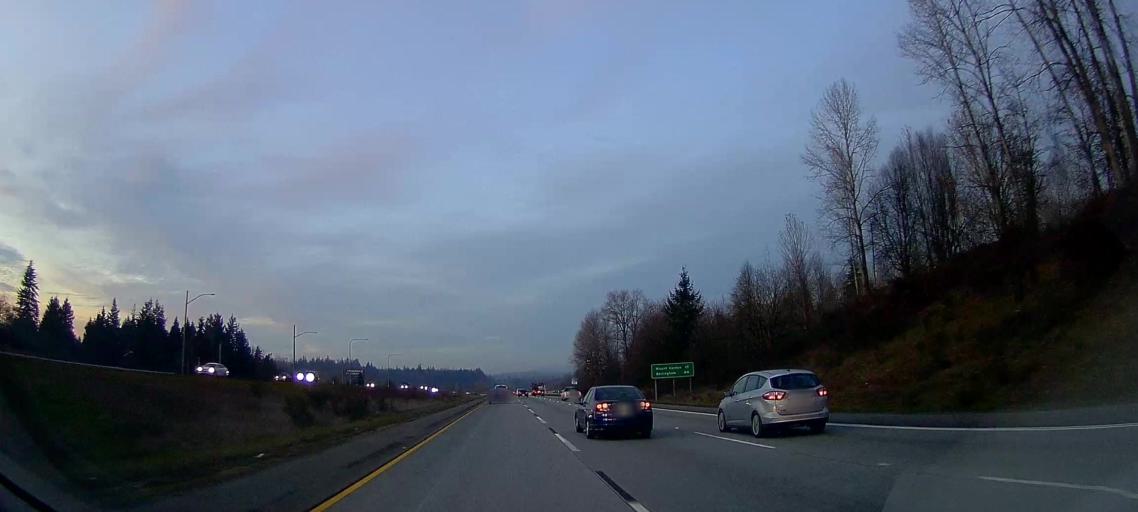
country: US
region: Washington
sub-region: Snohomish County
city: Smokey Point
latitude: 48.2043
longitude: -122.2129
